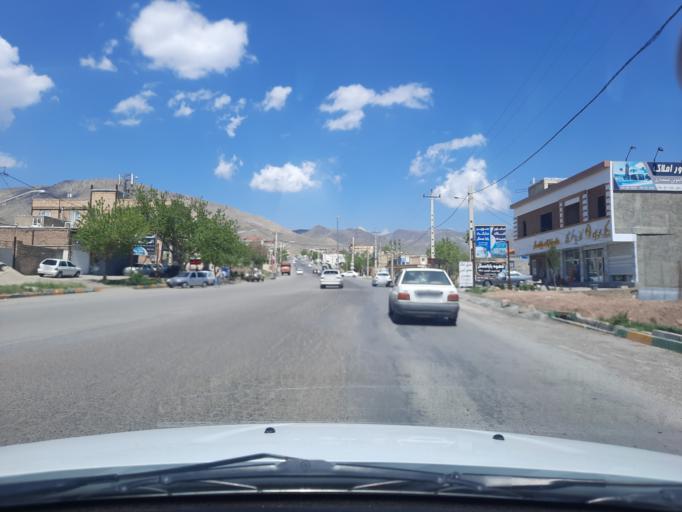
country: IR
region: Qazvin
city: Qazvin
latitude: 36.3304
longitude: 50.1498
